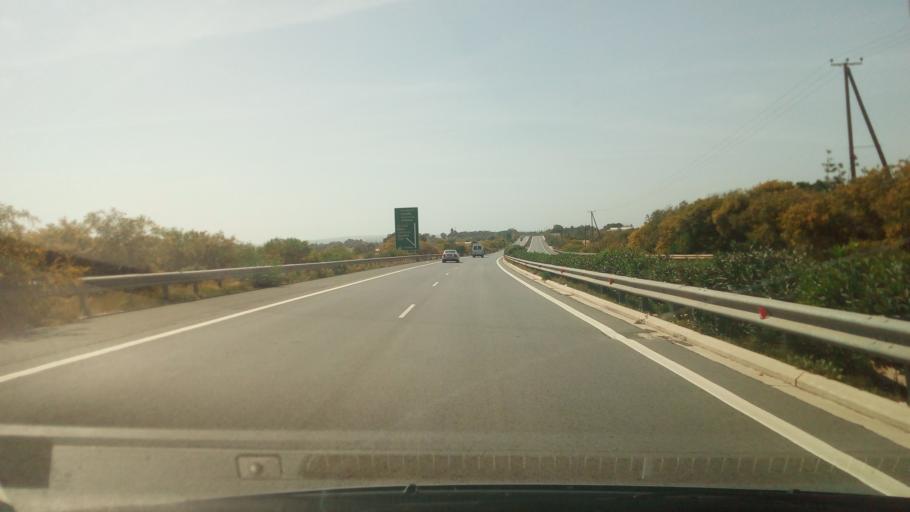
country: CY
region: Ammochostos
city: Liopetri
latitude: 34.9882
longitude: 33.9416
